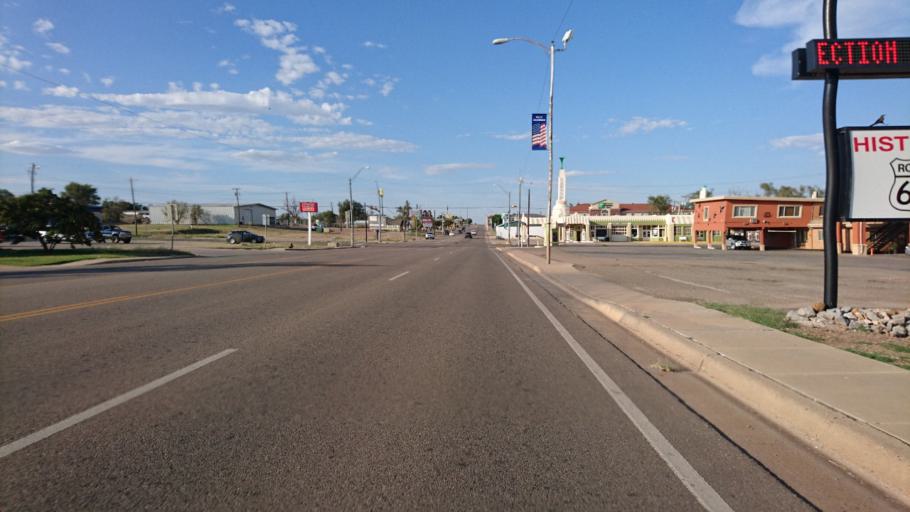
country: US
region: Texas
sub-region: Wheeler County
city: Shamrock
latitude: 35.2256
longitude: -100.2491
